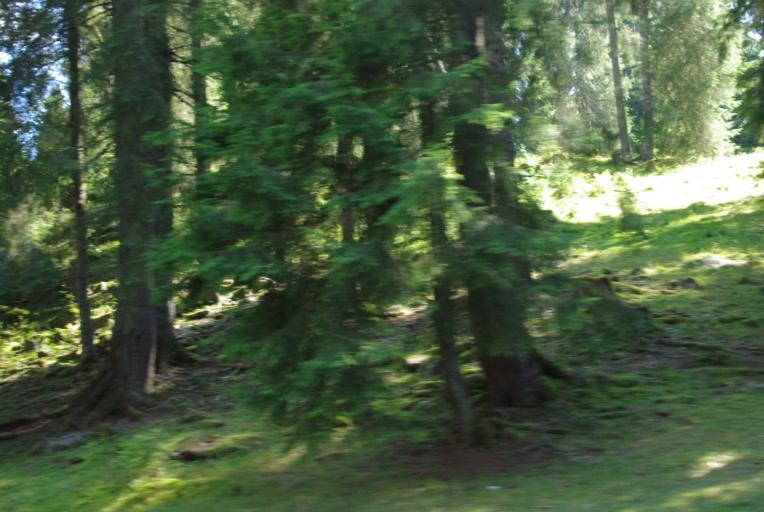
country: RO
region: Alba
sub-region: Comuna Arieseni
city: Arieseni
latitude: 46.5957
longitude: 22.7241
